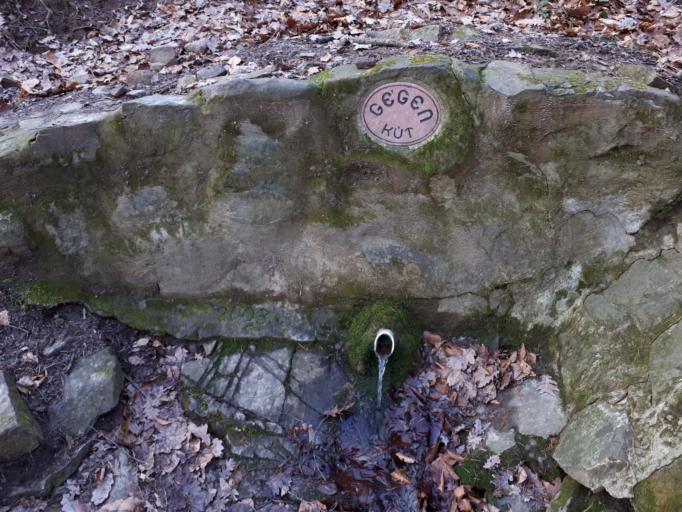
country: HU
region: Baranya
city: Pecs
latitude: 46.0998
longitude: 18.1714
